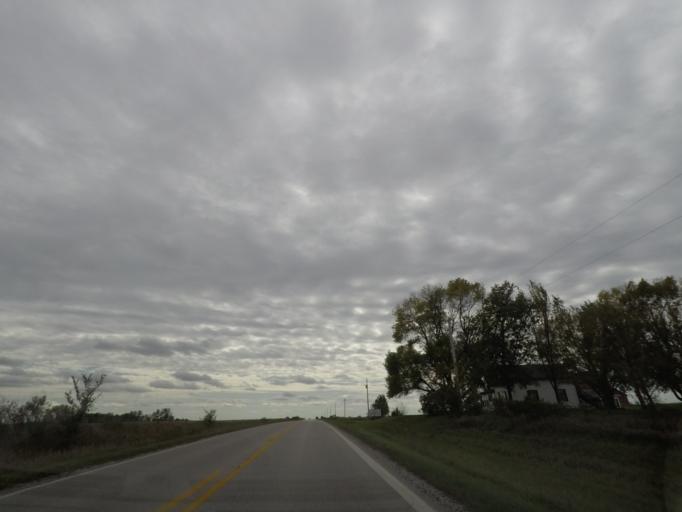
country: US
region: Iowa
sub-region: Story County
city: Huxley
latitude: 41.8626
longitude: -93.5317
